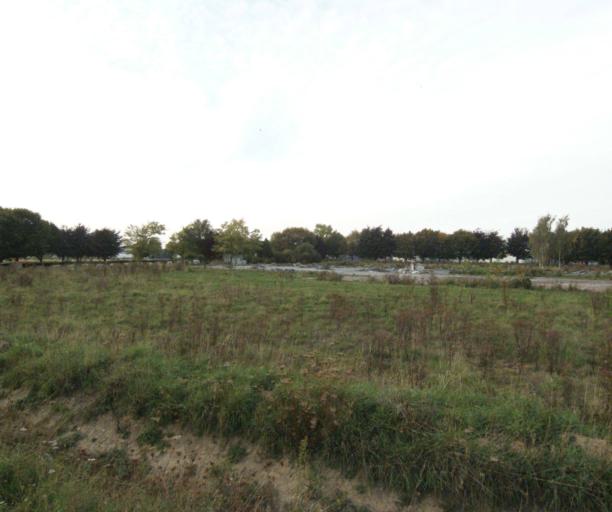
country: FR
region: Nord-Pas-de-Calais
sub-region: Departement du Nord
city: Avelin
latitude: 50.5463
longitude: 3.0609
